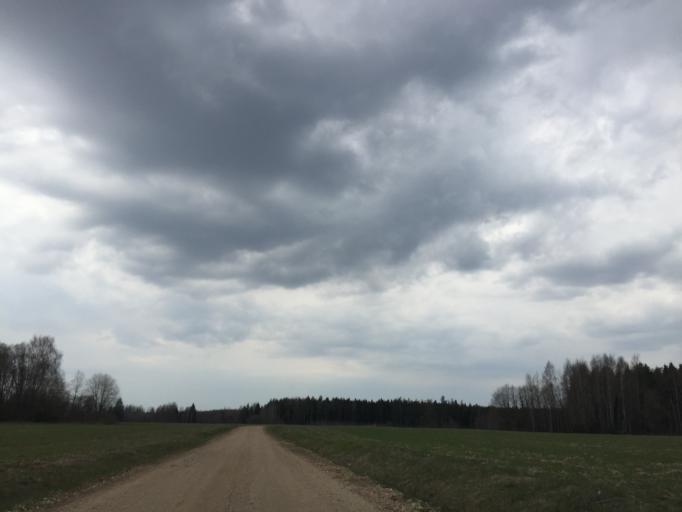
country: EE
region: Vorumaa
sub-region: Antsla vald
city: Vana-Antsla
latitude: 57.9386
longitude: 26.7275
